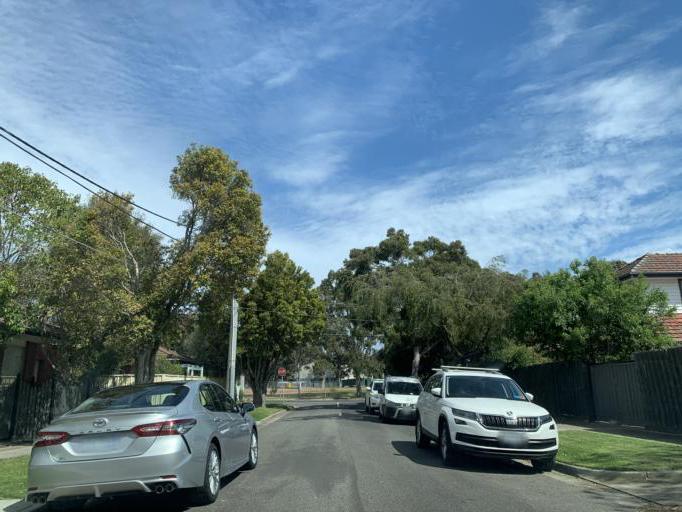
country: AU
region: Victoria
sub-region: Bayside
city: Hampton East
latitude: -37.9379
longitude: 145.0181
